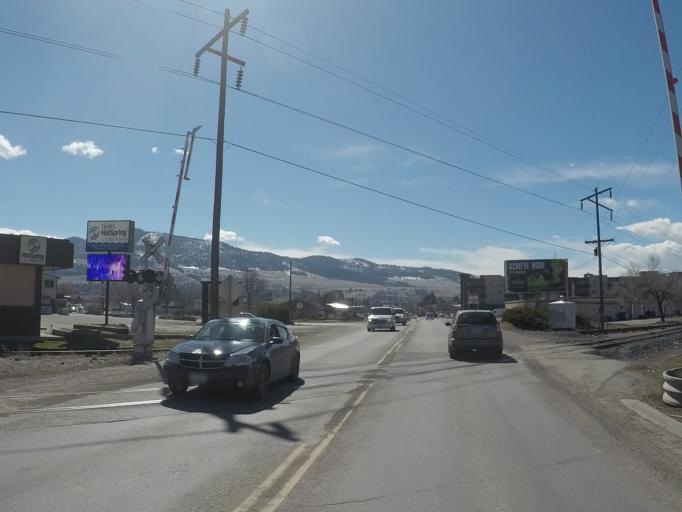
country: US
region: Montana
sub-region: Missoula County
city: Missoula
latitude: 46.8588
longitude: -114.0187
